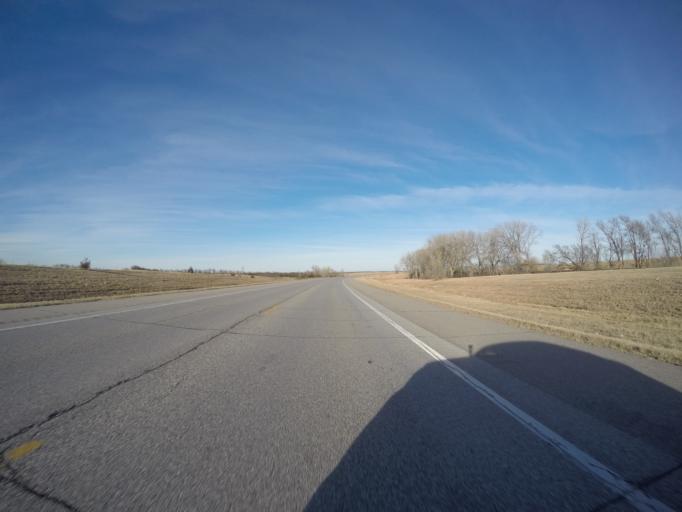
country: US
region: Kansas
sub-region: Marion County
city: Peabody
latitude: 38.1418
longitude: -97.2301
